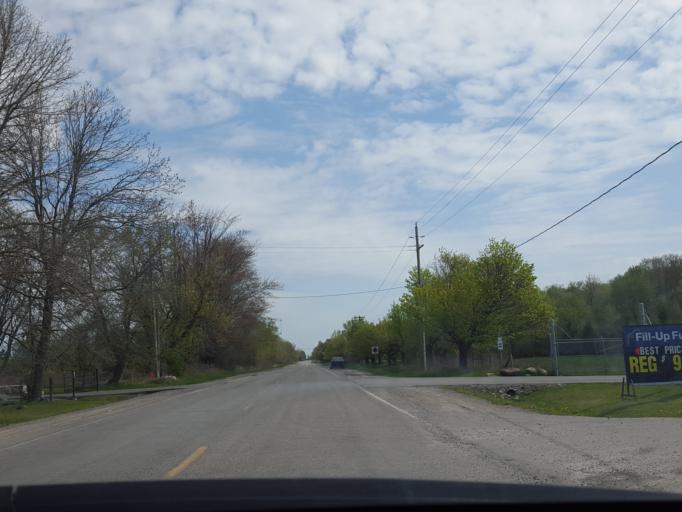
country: CA
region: Ontario
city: Uxbridge
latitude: 44.1871
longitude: -78.8858
